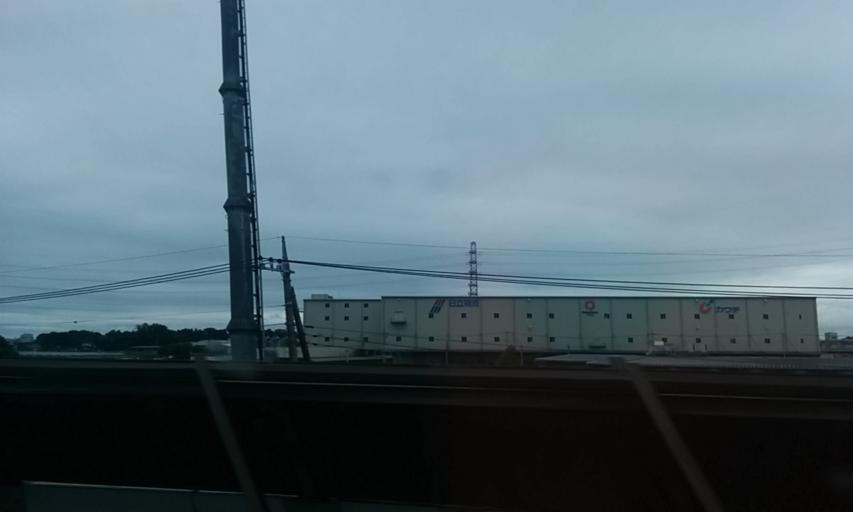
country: JP
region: Tochigi
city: Kaminokawa
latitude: 36.4184
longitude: 139.8635
